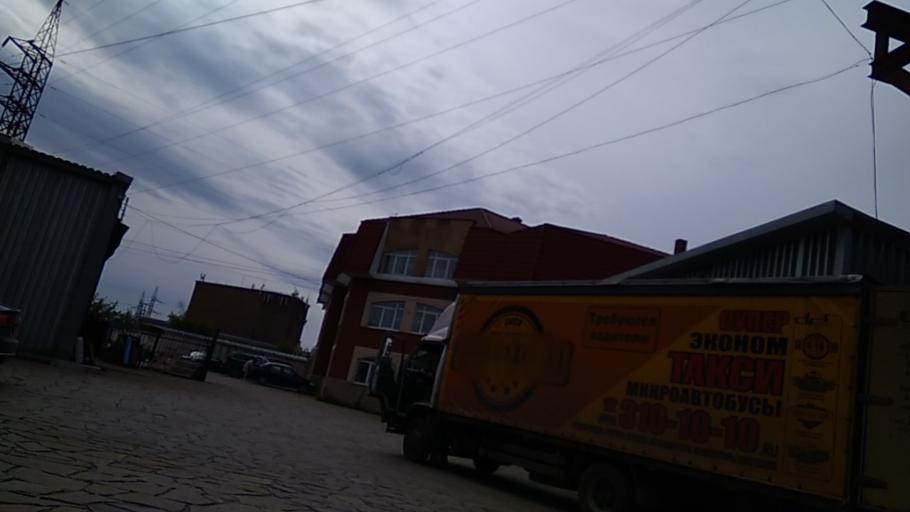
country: RU
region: Sverdlovsk
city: Yekaterinburg
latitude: 56.8835
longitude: 60.6217
